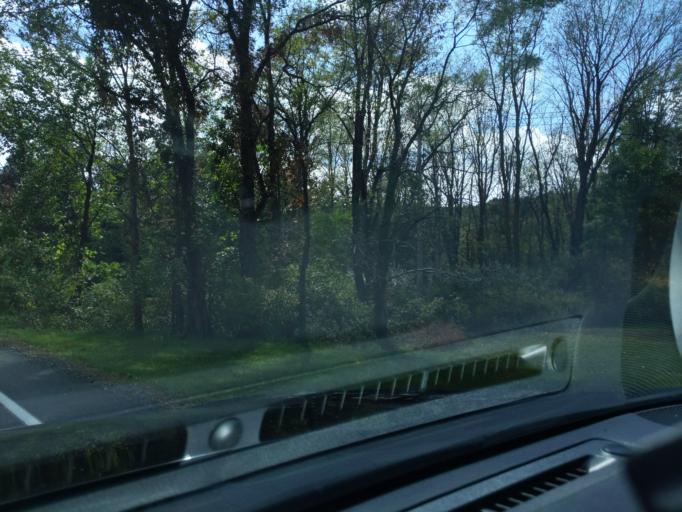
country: US
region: Pennsylvania
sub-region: Blair County
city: Altoona
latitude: 40.4920
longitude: -78.4481
